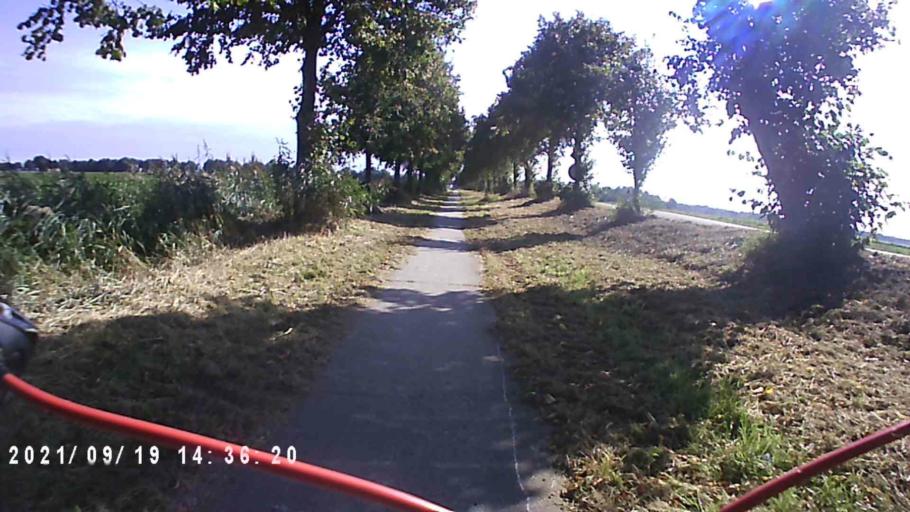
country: NL
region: Groningen
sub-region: Gemeente Vlagtwedde
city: Vlagtwedde
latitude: 53.1356
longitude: 7.1543
